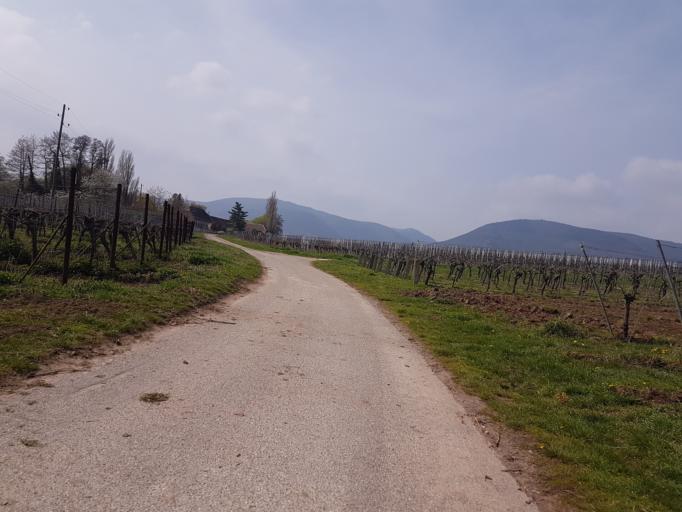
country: DE
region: Rheinland-Pfalz
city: Roschbach
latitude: 49.2592
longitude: 8.1178
